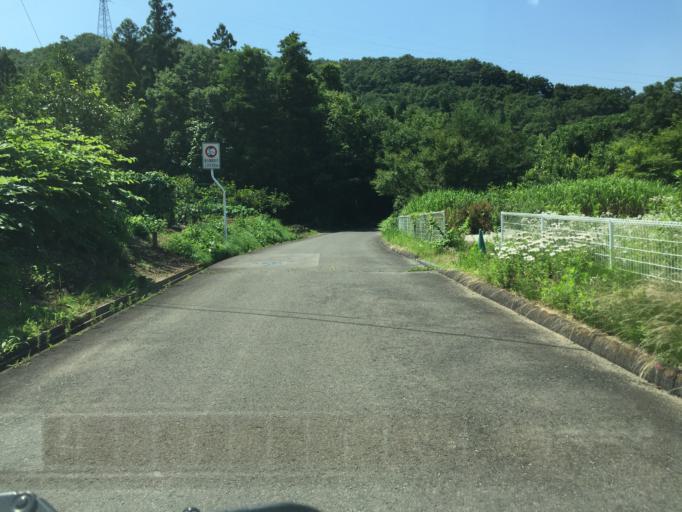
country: JP
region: Fukushima
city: Fukushima-shi
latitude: 37.7115
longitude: 140.4613
